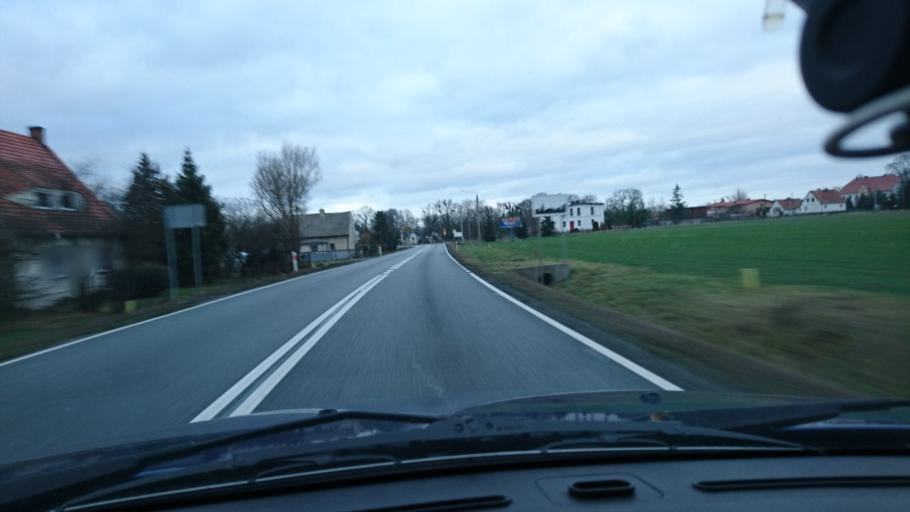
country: PL
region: Opole Voivodeship
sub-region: Powiat kluczborski
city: Byczyna
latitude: 51.0599
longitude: 18.1994
